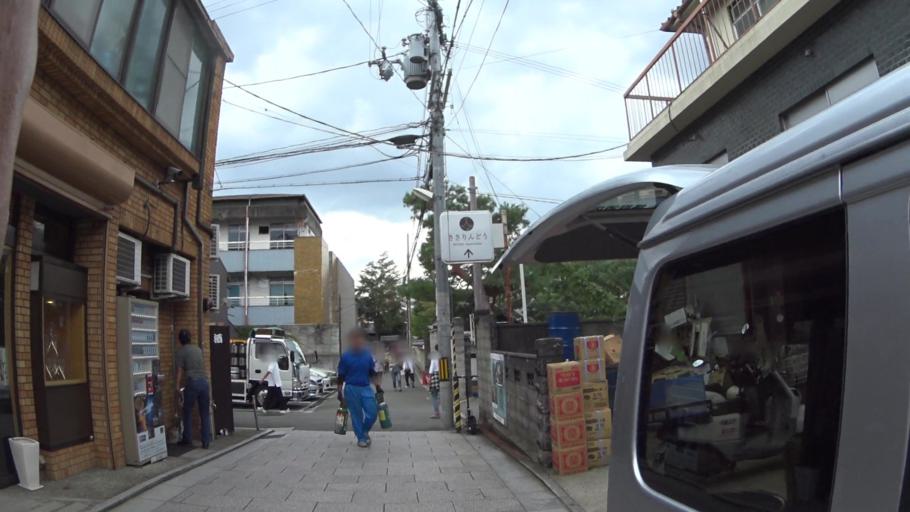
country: JP
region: Kyoto
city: Kyoto
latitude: 35.0026
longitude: 135.7747
